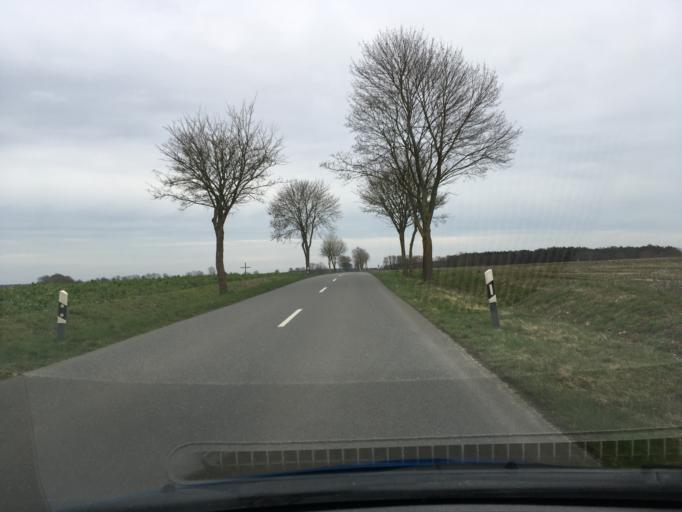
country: DE
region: Lower Saxony
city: Emmendorf
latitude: 53.0029
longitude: 10.6161
